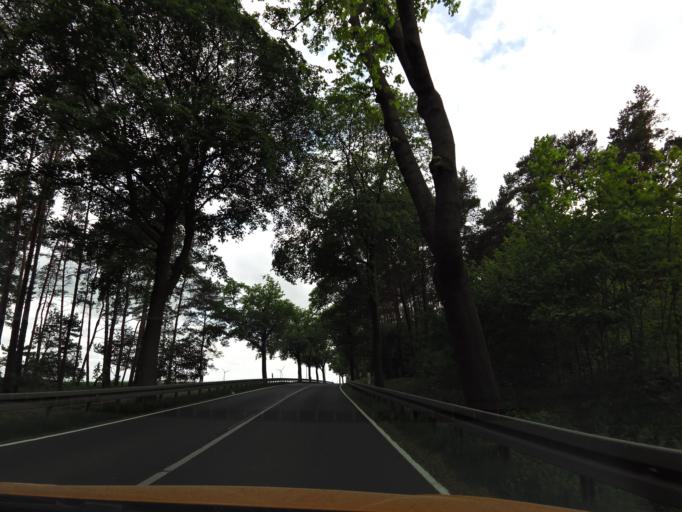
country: DE
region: Brandenburg
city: Niemegk
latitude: 52.0858
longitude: 12.7394
